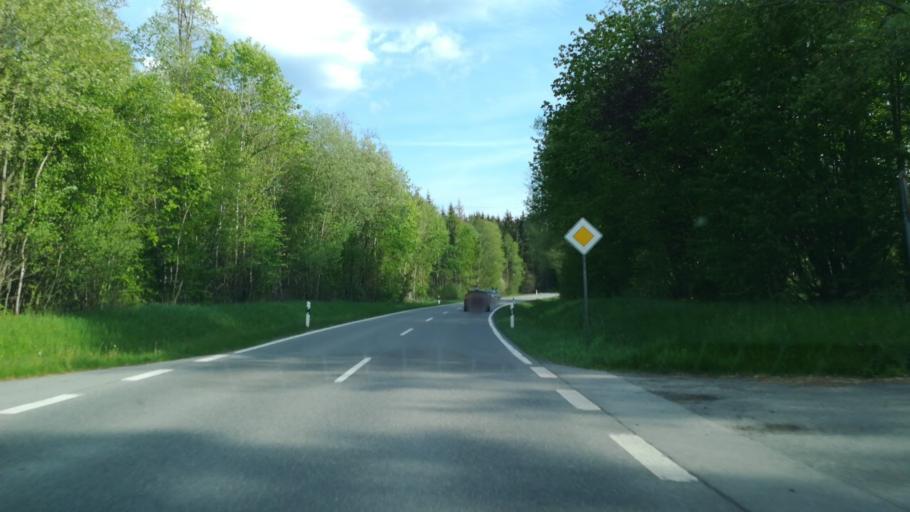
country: DE
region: Baden-Wuerttemberg
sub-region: Freiburg Region
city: Muhlingen
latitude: 47.9226
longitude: 9.0549
